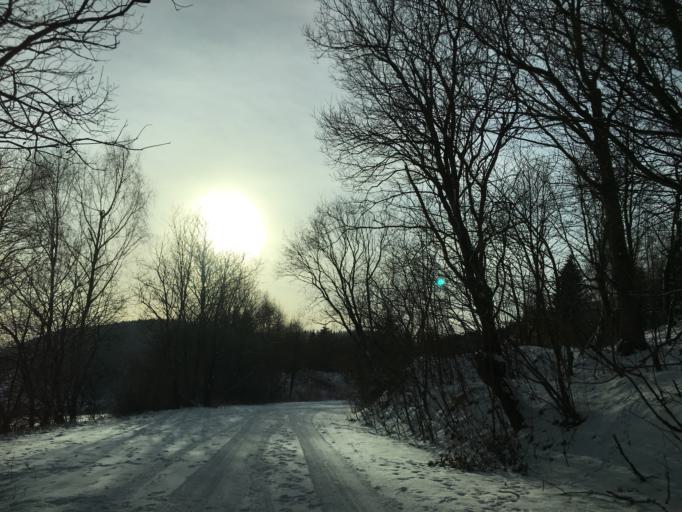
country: PL
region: Lower Silesian Voivodeship
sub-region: Powiat walbrzyski
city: Gluszyca Gorna
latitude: 50.6656
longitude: 16.3566
